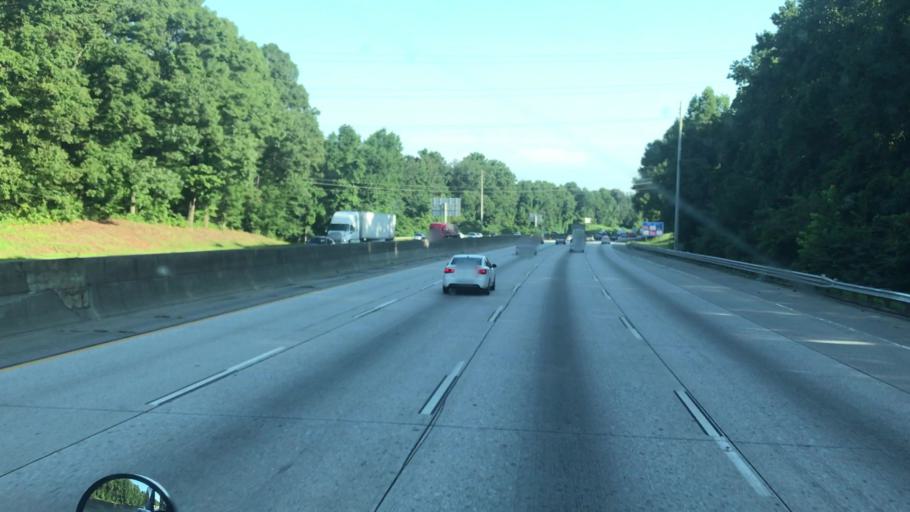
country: US
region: Georgia
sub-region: Fulton County
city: College Park
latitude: 33.6420
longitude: -84.4958
